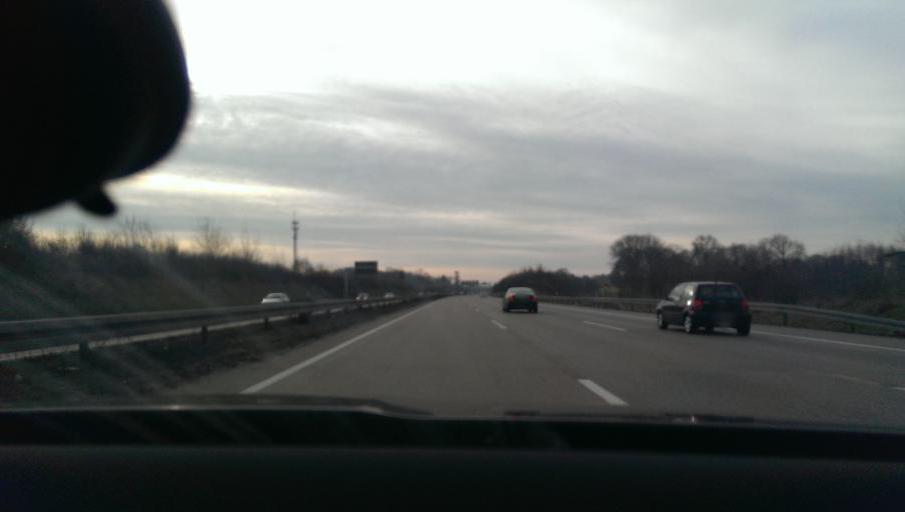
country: DE
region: Lower Saxony
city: Isernhagen Farster Bauerschaft
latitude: 52.4806
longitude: 9.8483
